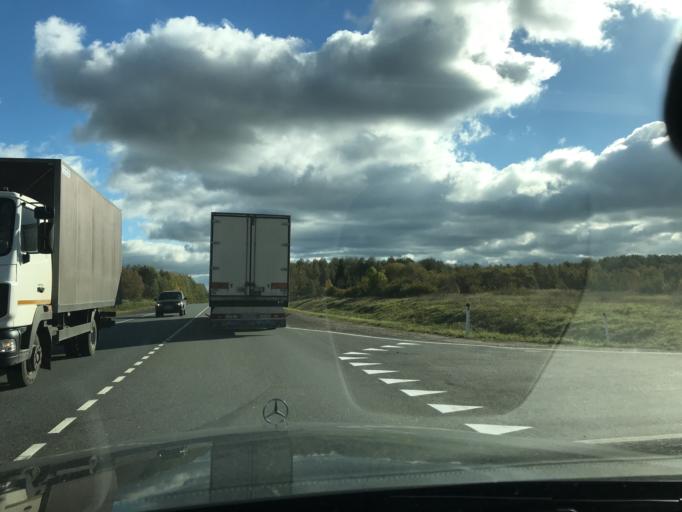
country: RU
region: Pskov
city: Ostrov
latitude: 57.0705
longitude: 28.5669
